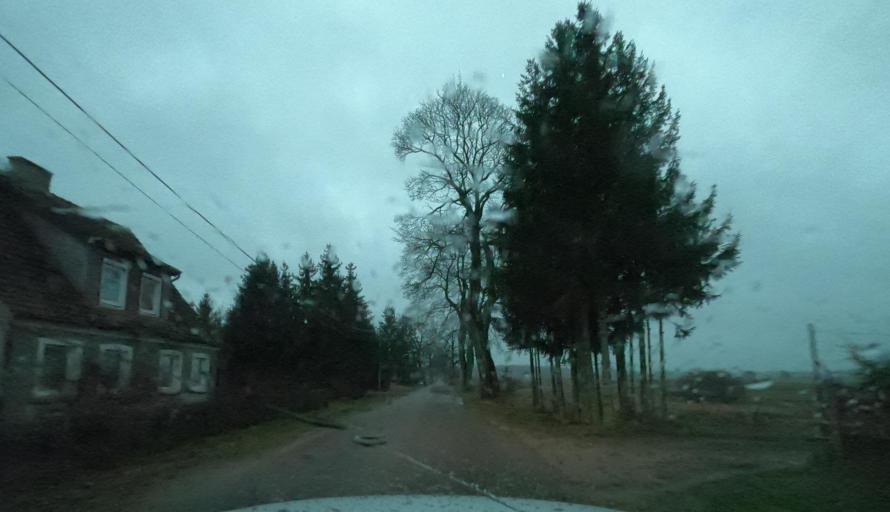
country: PL
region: West Pomeranian Voivodeship
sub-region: Powiat szczecinecki
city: Borne Sulinowo
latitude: 53.6677
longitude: 16.4899
